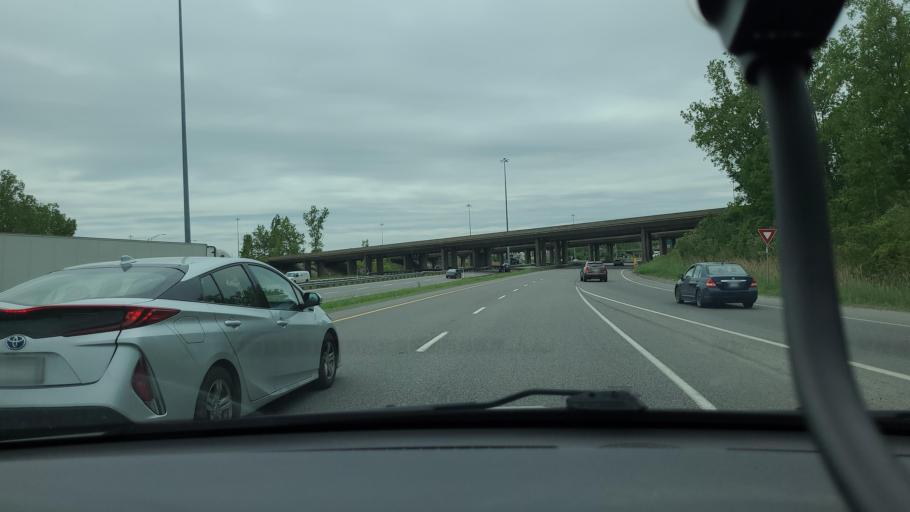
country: CA
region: Quebec
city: Bois-des-Filion
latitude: 45.6741
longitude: -73.7634
